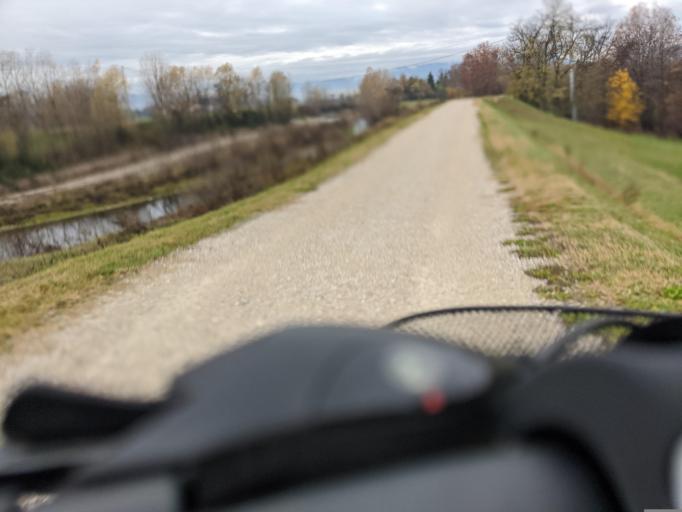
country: IT
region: Veneto
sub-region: Provincia di Vicenza
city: Dueville
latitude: 45.6160
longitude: 11.5360
